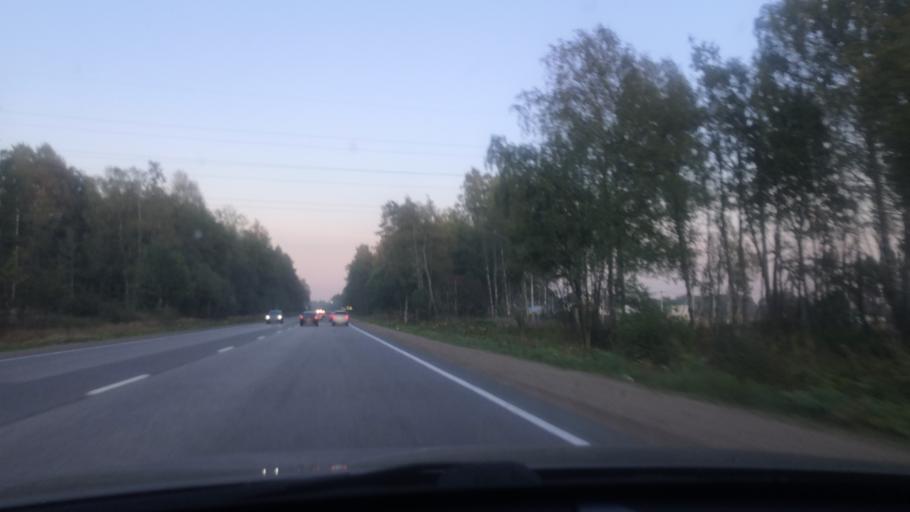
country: RU
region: St.-Petersburg
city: Beloostrov
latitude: 60.1986
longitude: 29.9991
